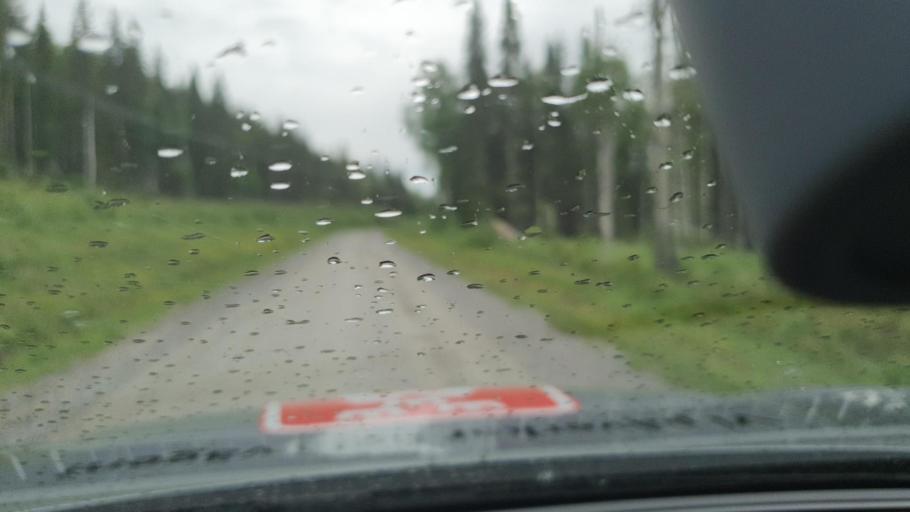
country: SE
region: Norrbotten
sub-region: Kalix Kommun
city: Rolfs
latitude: 66.0170
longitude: 23.1112
